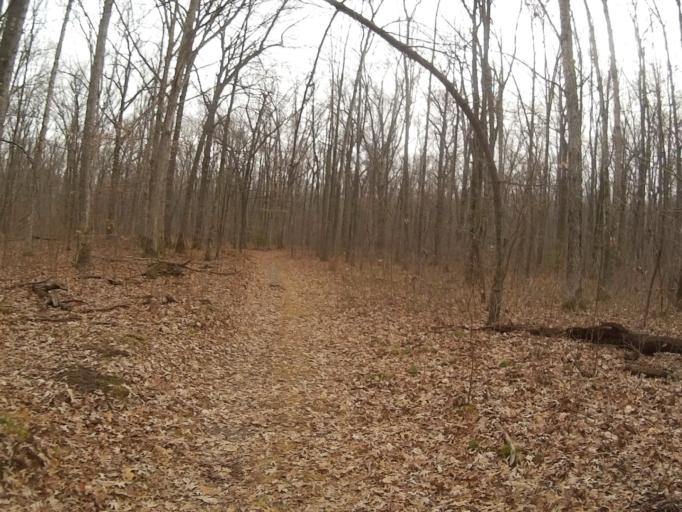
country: US
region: Pennsylvania
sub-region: Centre County
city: Park Forest Village
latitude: 40.7899
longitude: -77.9261
